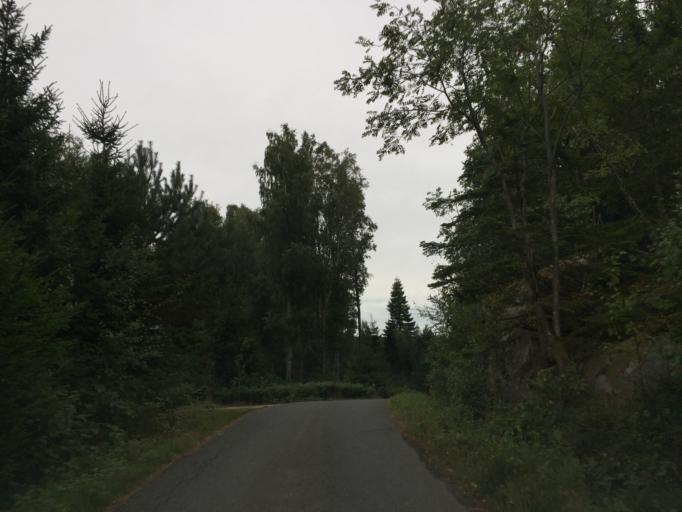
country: NO
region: Ostfold
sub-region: Hvaler
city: Skjaerhalden
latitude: 59.0787
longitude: 11.0053
